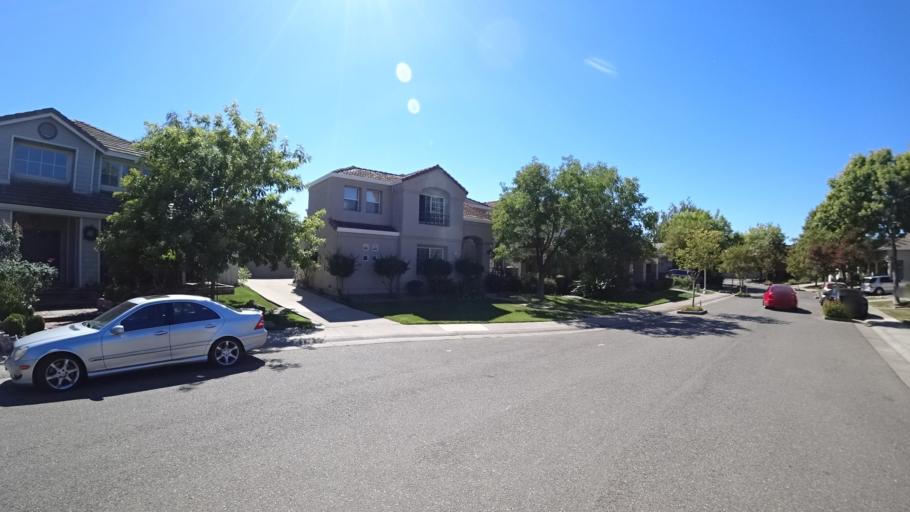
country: US
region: California
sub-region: Sacramento County
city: Laguna
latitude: 38.4171
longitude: -121.4582
